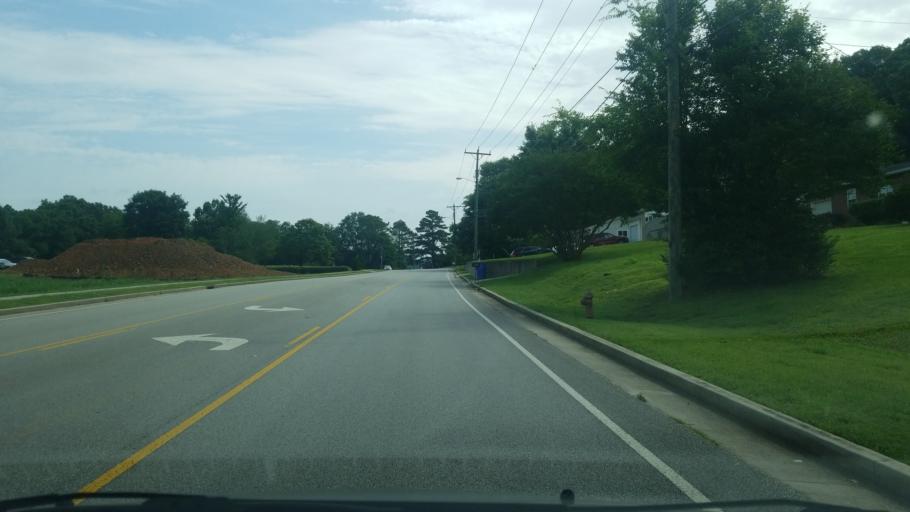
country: US
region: Tennessee
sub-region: Hamilton County
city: Collegedale
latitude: 35.0443
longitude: -85.0442
